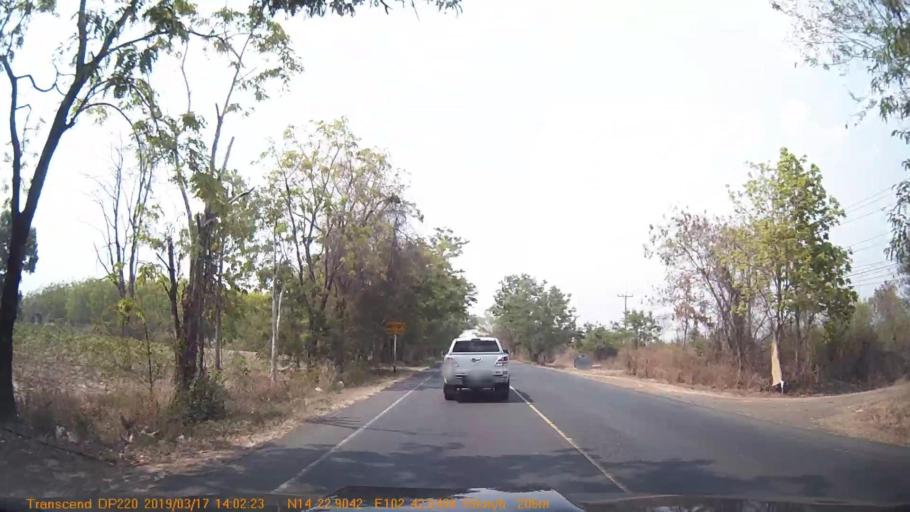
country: TH
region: Buriram
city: Pa Kham
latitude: 14.3819
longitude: 102.7107
